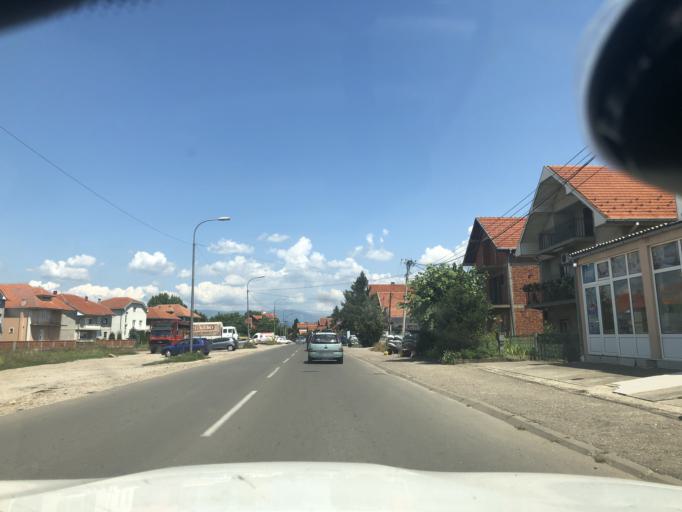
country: RS
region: Central Serbia
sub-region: Jablanicki Okrug
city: Leskovac
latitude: 42.9902
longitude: 21.9271
